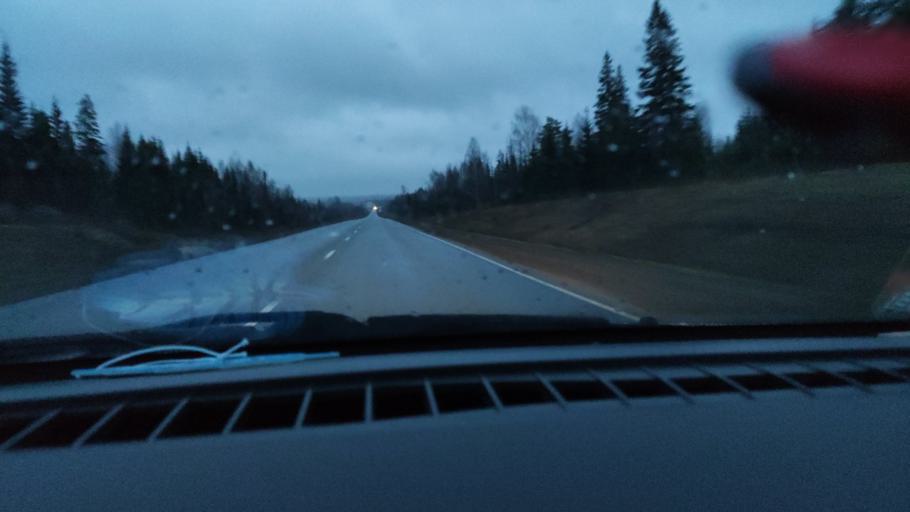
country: RU
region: Udmurtiya
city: Mozhga
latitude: 56.3305
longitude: 52.3071
